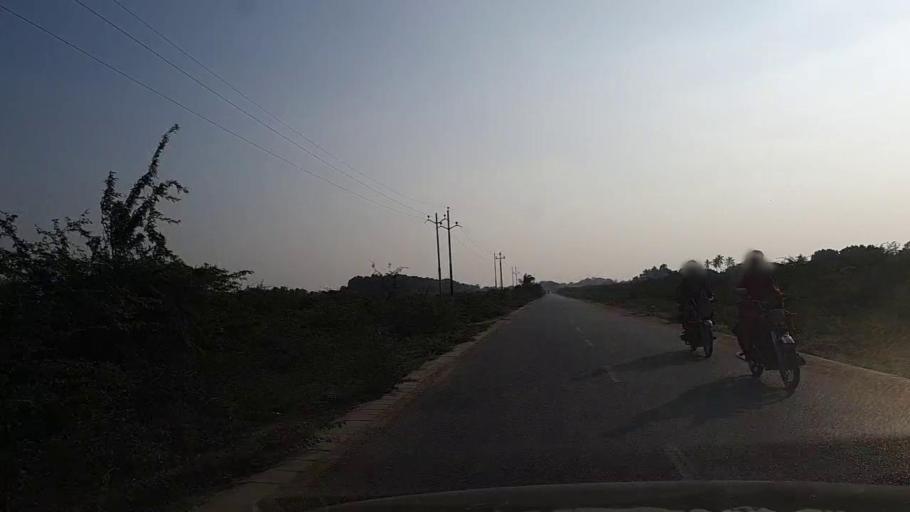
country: PK
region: Sindh
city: Gharo
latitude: 24.7881
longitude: 67.5146
